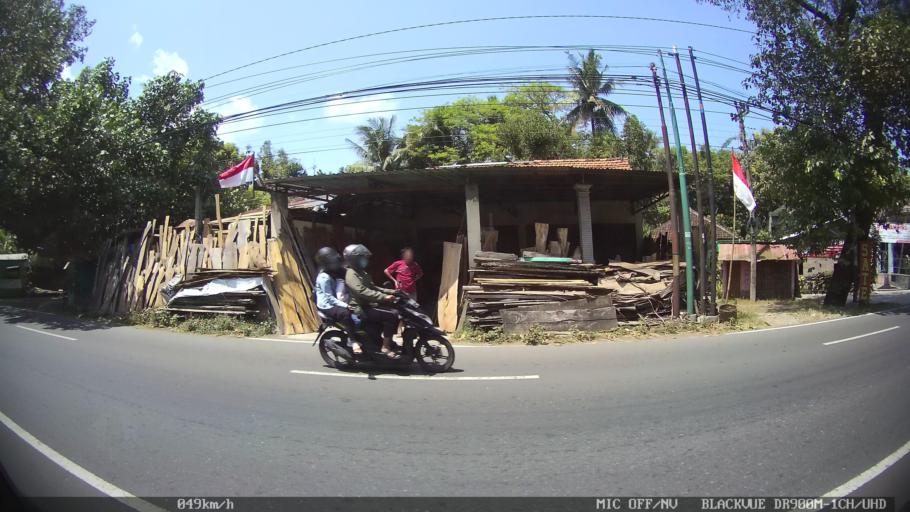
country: ID
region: Daerah Istimewa Yogyakarta
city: Bambanglipuro
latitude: -7.9318
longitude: 110.2716
